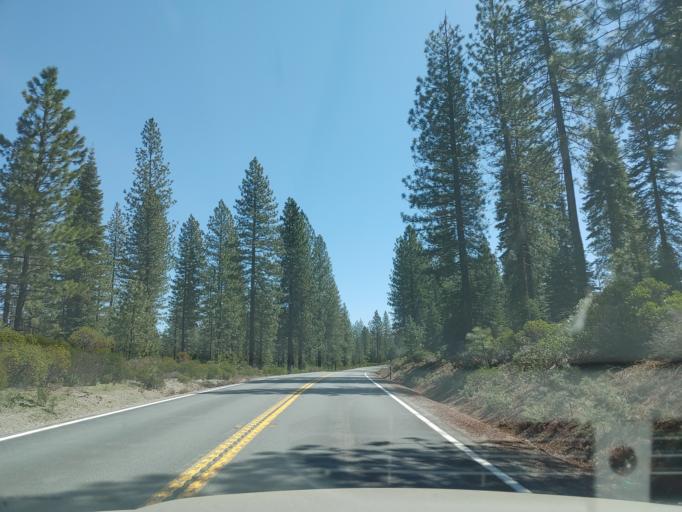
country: US
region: California
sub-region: Siskiyou County
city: McCloud
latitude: 41.2661
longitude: -121.8571
